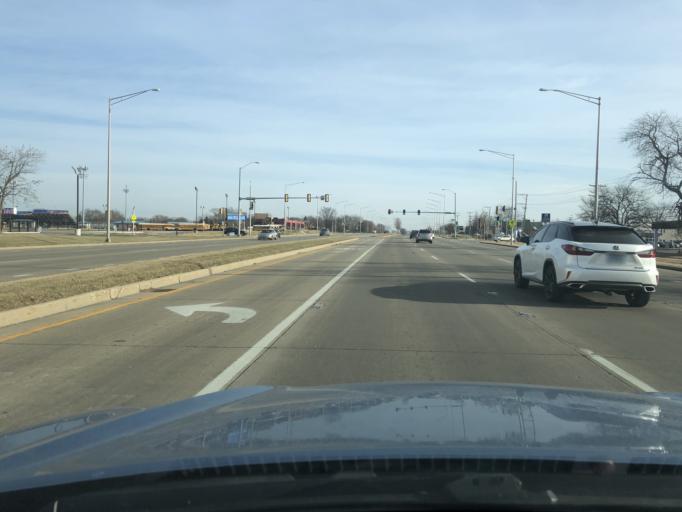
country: US
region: Illinois
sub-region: Cook County
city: Hoffman Estates
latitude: 42.0519
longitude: -88.1092
